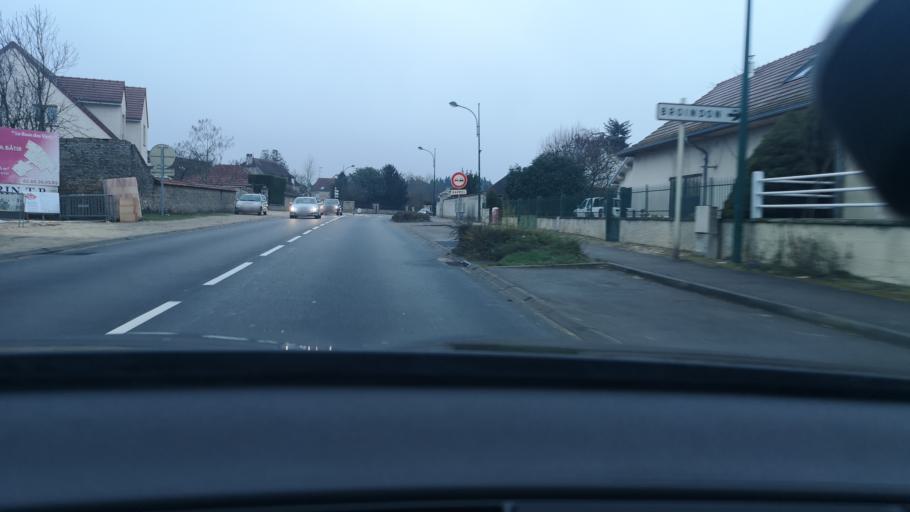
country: FR
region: Bourgogne
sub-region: Departement de la Cote-d'Or
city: Fenay
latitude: 47.1947
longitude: 5.0814
